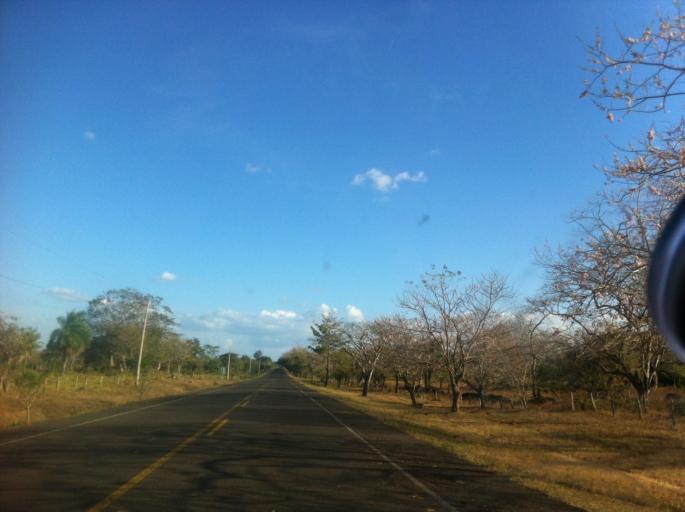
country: NI
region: Rio San Juan
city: Morrito
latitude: 11.7793
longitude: -85.0185
